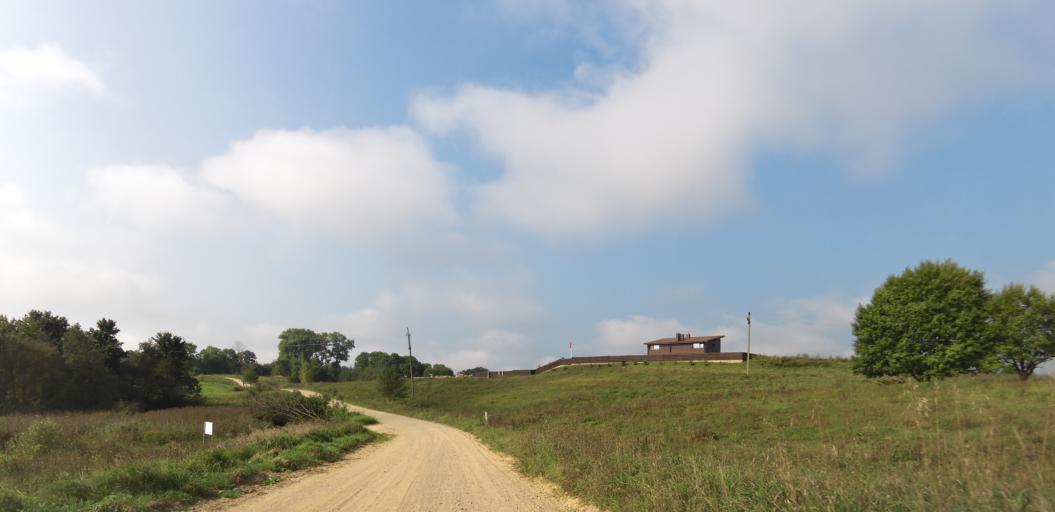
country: LT
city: Grigiskes
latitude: 54.7682
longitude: 25.0497
